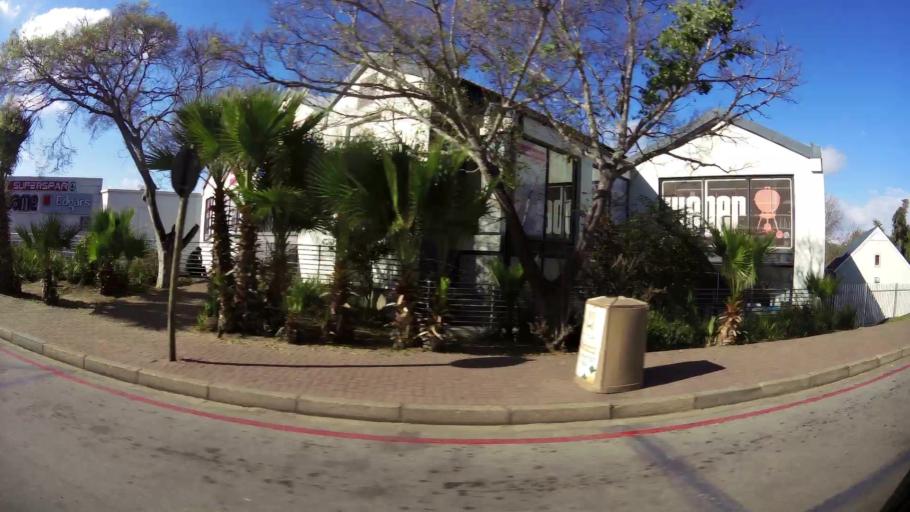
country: ZA
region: Western Cape
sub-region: Eden District Municipality
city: Knysna
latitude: -34.0353
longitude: 23.0429
